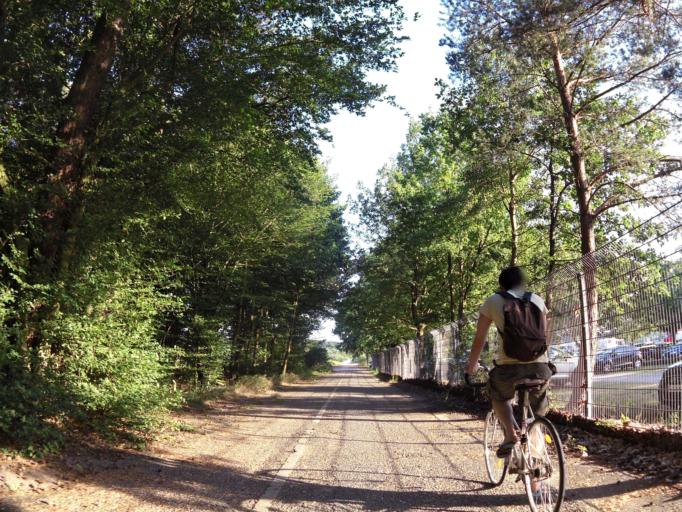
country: DE
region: Hesse
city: Morfelden-Walldorf
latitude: 50.0192
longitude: 8.6237
